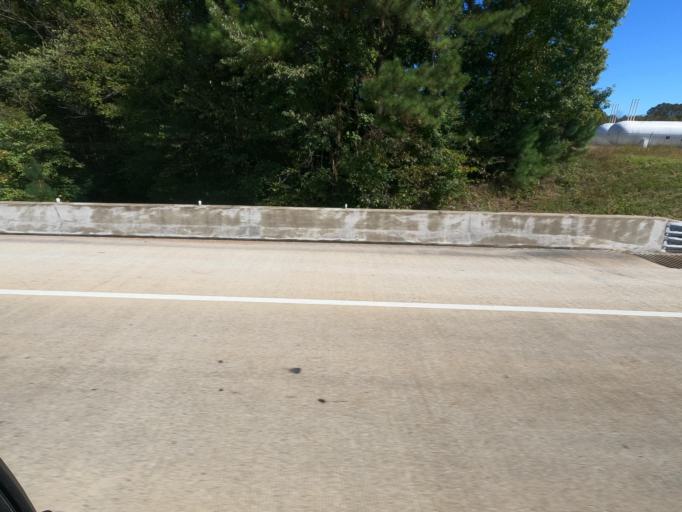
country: US
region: Tennessee
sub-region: Maury County
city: Mount Pleasant
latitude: 35.4072
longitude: -87.2811
